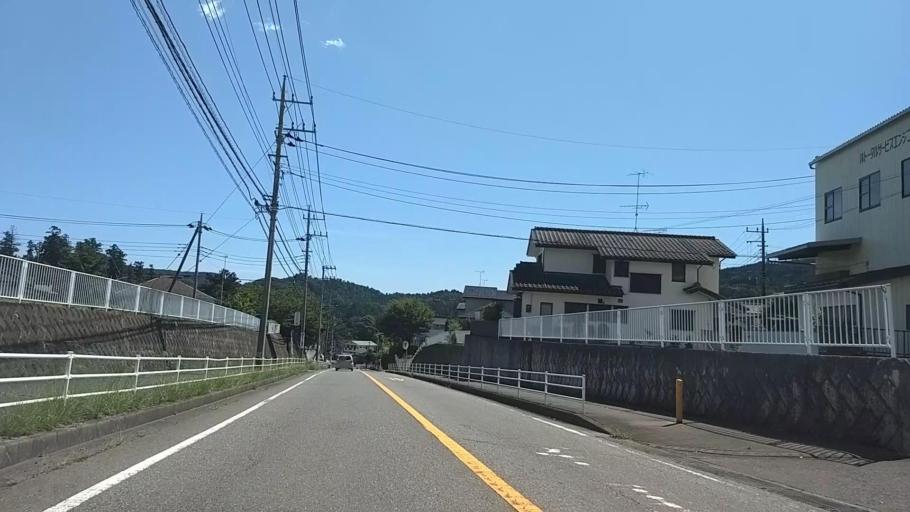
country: JP
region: Tokyo
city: Hachioji
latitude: 35.5680
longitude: 139.2426
